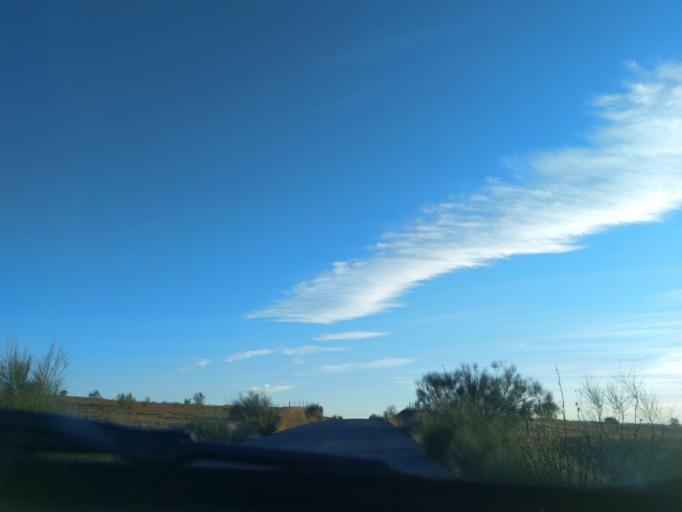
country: ES
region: Extremadura
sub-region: Provincia de Badajoz
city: Berlanga
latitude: 38.2703
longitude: -5.8223
